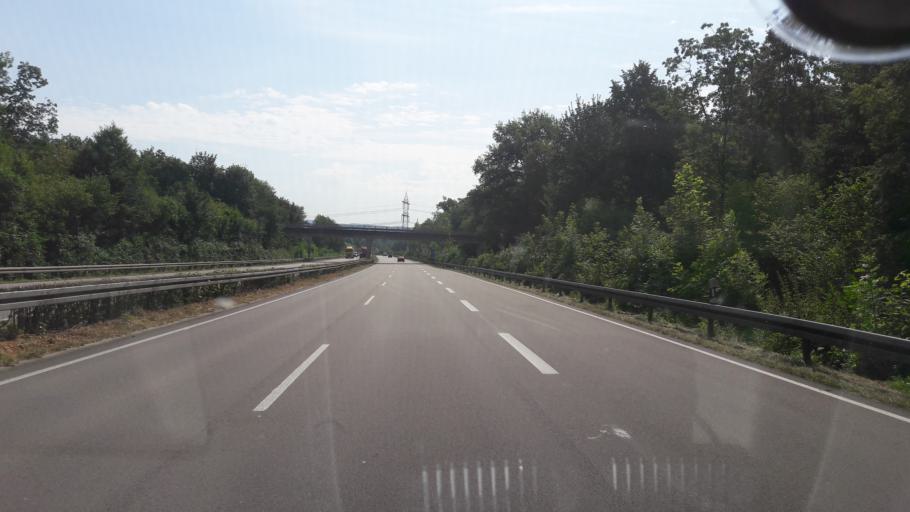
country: DE
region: Baden-Wuerttemberg
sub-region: Freiburg Region
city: Appenweier
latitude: 48.5343
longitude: 7.9402
